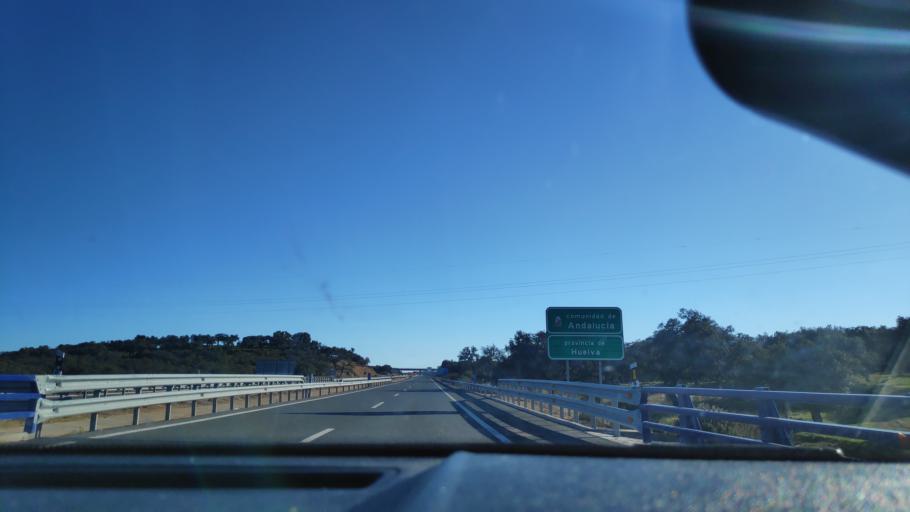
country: ES
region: Andalusia
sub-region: Provincia de Huelva
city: Santa Olalla del Cala
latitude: 37.9577
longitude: -6.2328
